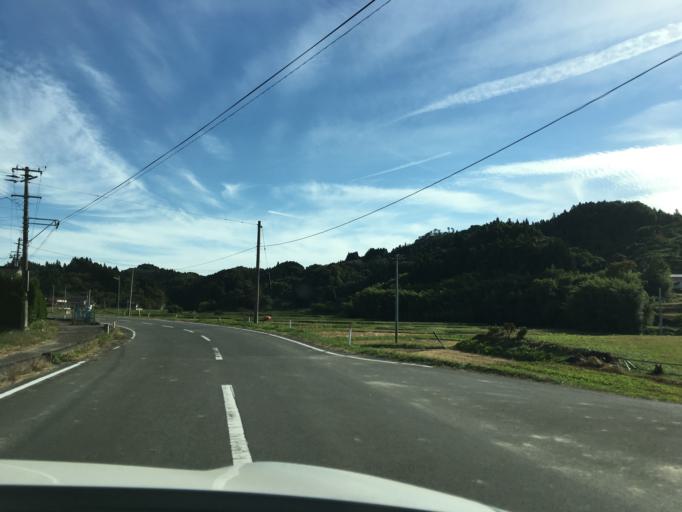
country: JP
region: Fukushima
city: Miharu
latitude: 37.3352
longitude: 140.4879
